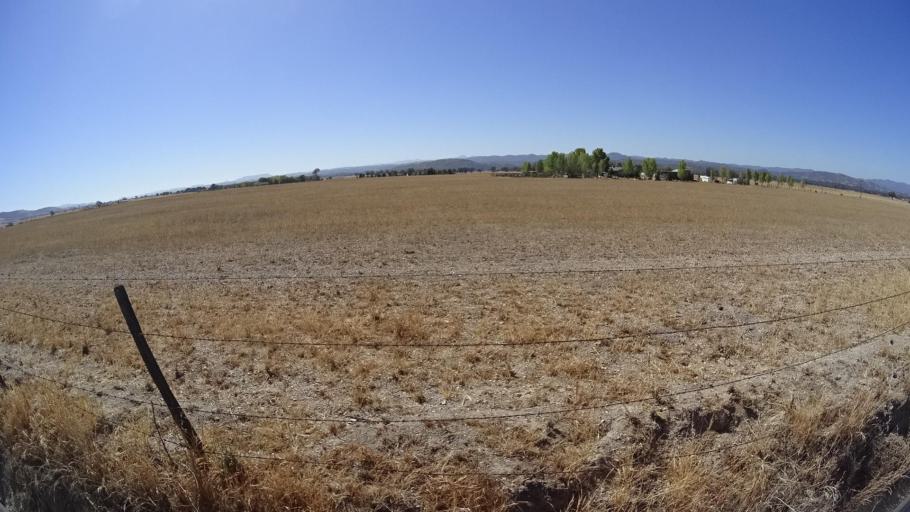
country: US
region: California
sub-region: Monterey County
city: King City
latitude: 35.9515
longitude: -121.0800
